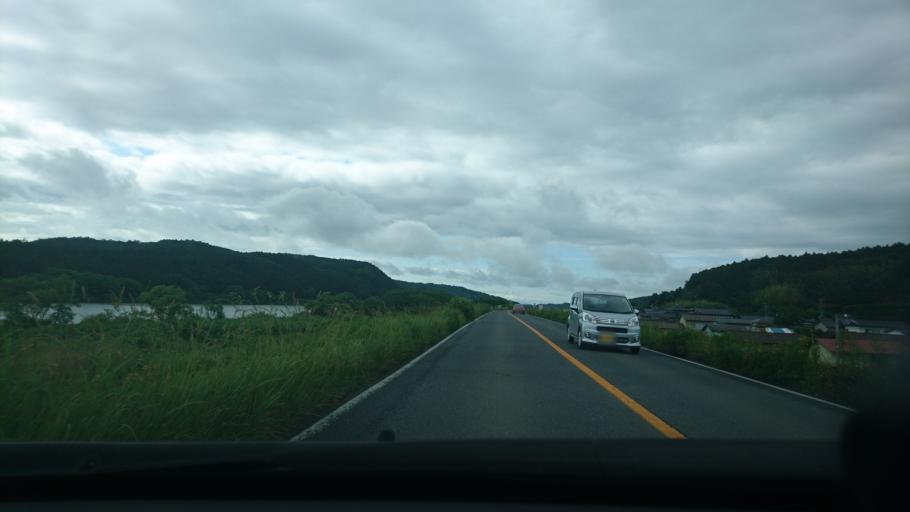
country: JP
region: Miyagi
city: Wakuya
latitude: 38.6201
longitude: 141.2971
